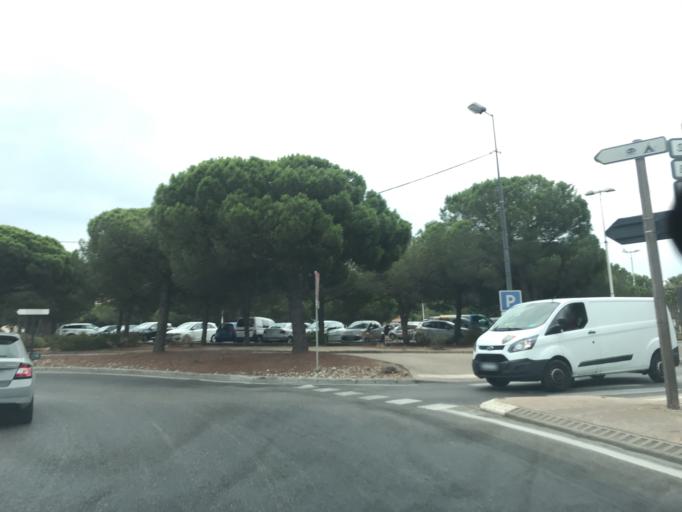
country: FR
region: Provence-Alpes-Cote d'Azur
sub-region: Departement du Var
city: La Seyne-sur-Mer
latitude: 43.0793
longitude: 5.8987
